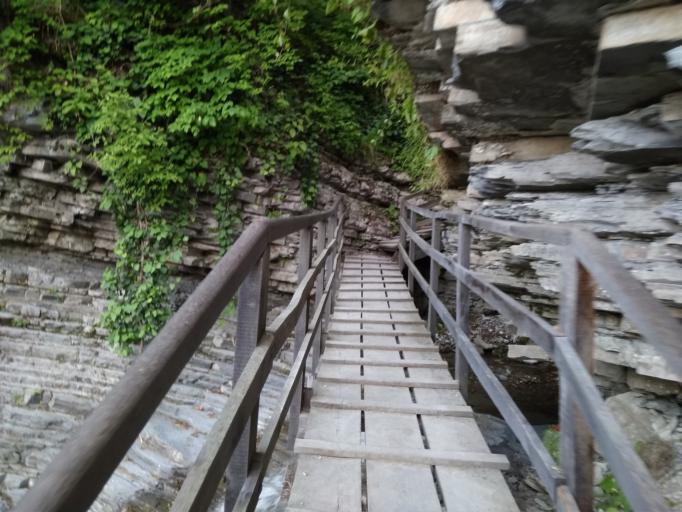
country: RU
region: Krasnodarskiy
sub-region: Sochi City
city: Lazarevskoye
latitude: 44.0005
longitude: 39.3910
